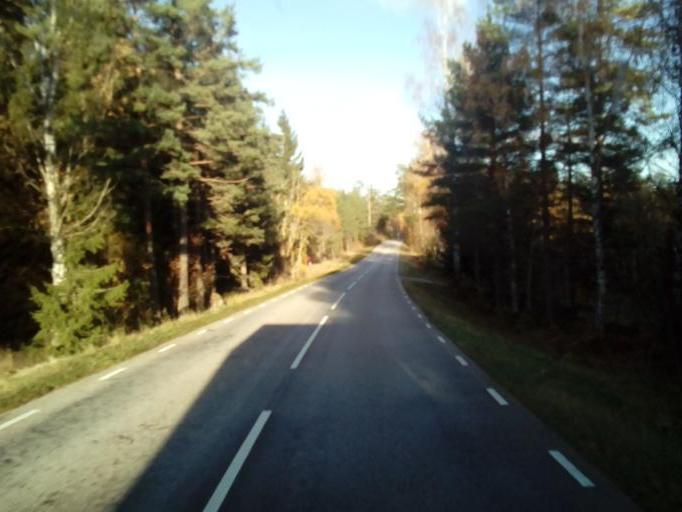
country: SE
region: Kalmar
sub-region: Vasterviks Kommun
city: Ankarsrum
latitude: 57.7700
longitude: 16.1409
